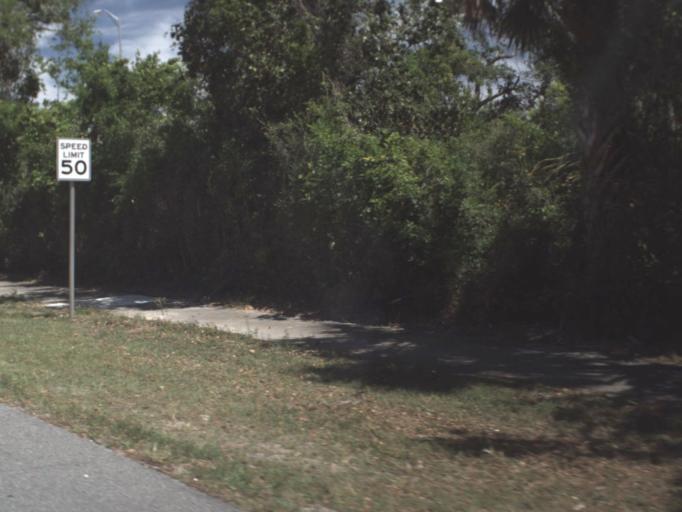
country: US
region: Florida
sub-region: Flagler County
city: Palm Coast
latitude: 29.5748
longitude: -81.1857
